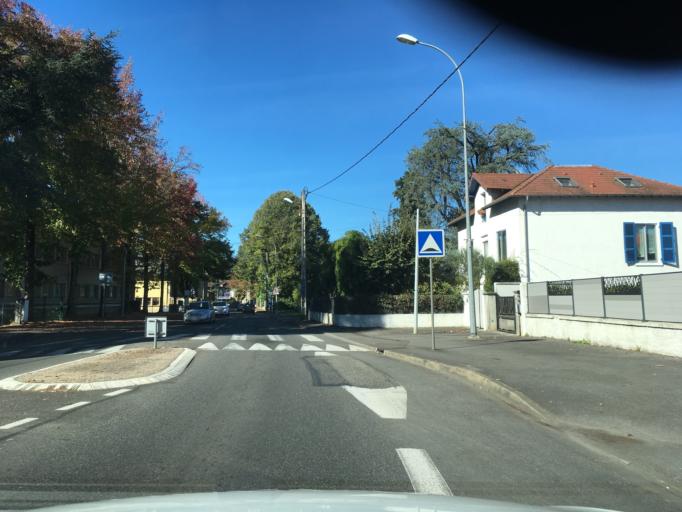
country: FR
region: Aquitaine
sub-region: Departement des Pyrenees-Atlantiques
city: Pau
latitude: 43.3088
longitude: -0.3416
